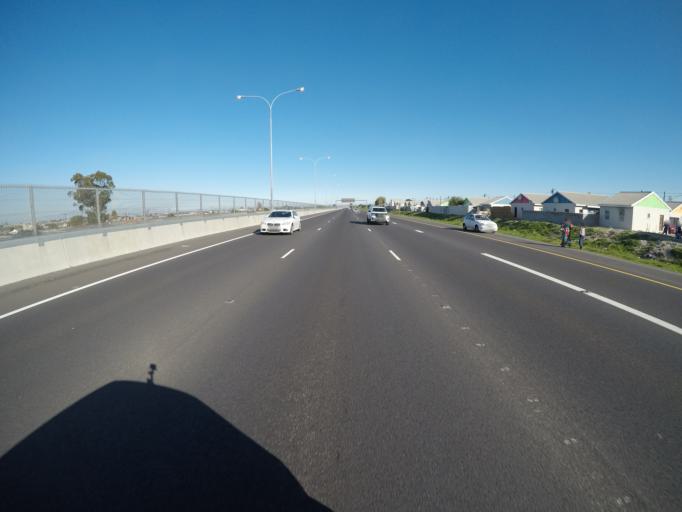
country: ZA
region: Western Cape
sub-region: City of Cape Town
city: Kraaifontein
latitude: -33.9609
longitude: 18.6560
